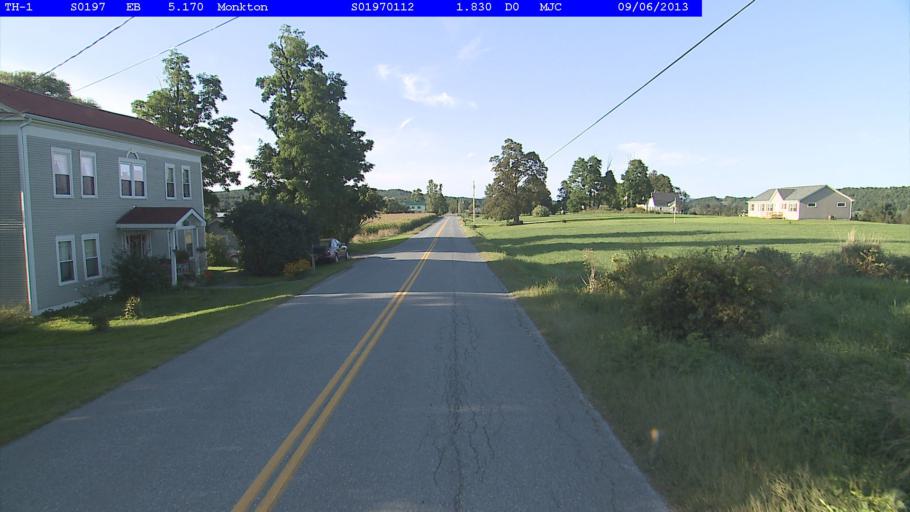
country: US
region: Vermont
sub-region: Addison County
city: Vergennes
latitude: 44.2089
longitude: -73.1632
